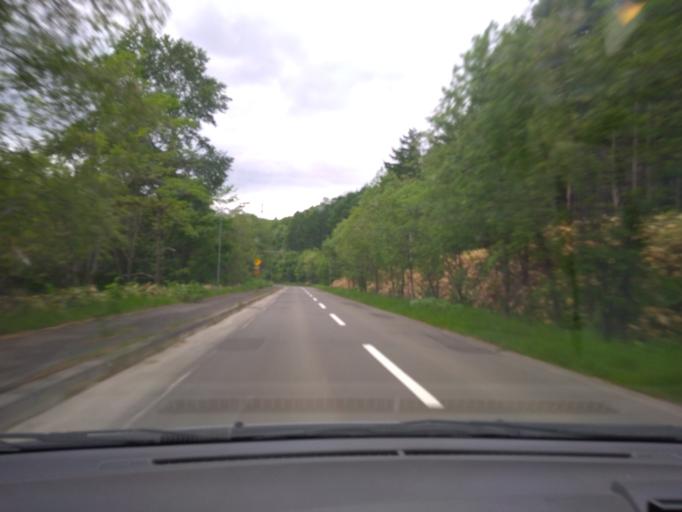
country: JP
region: Hokkaido
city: Shimo-furano
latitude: 43.1567
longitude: 142.5043
